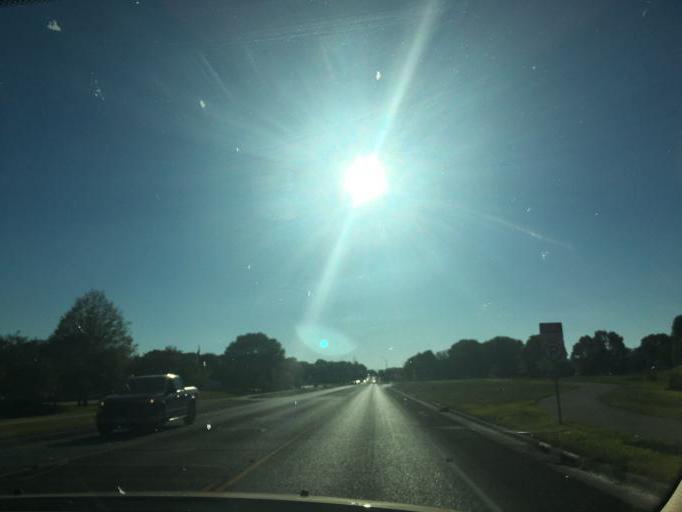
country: US
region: Minnesota
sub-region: Olmsted County
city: Rochester
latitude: 44.0795
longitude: -92.5256
